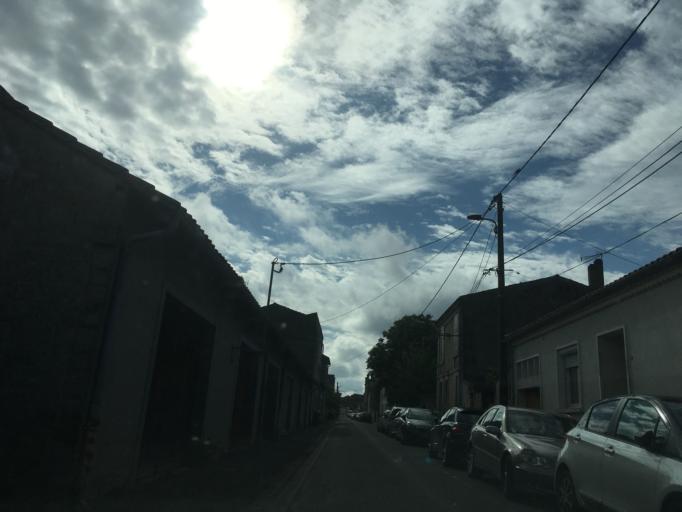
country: FR
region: Poitou-Charentes
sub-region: Departement de la Charente
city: Cognac
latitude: 45.6879
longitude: -0.3332
